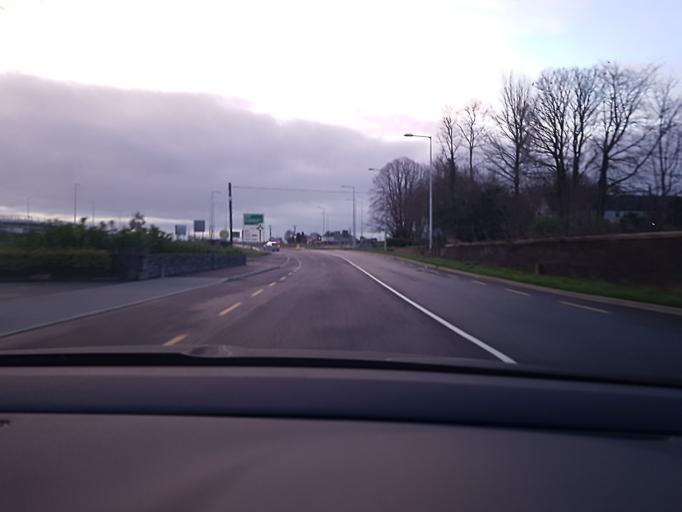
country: IE
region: Connaught
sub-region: County Galway
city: Tuam
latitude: 53.5278
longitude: -8.8723
